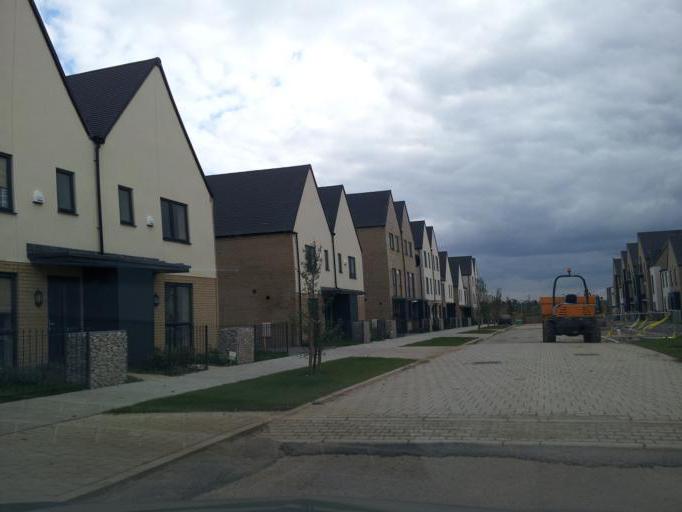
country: GB
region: England
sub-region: Milton Keynes
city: Shenley Church End
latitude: 51.9945
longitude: -0.8010
